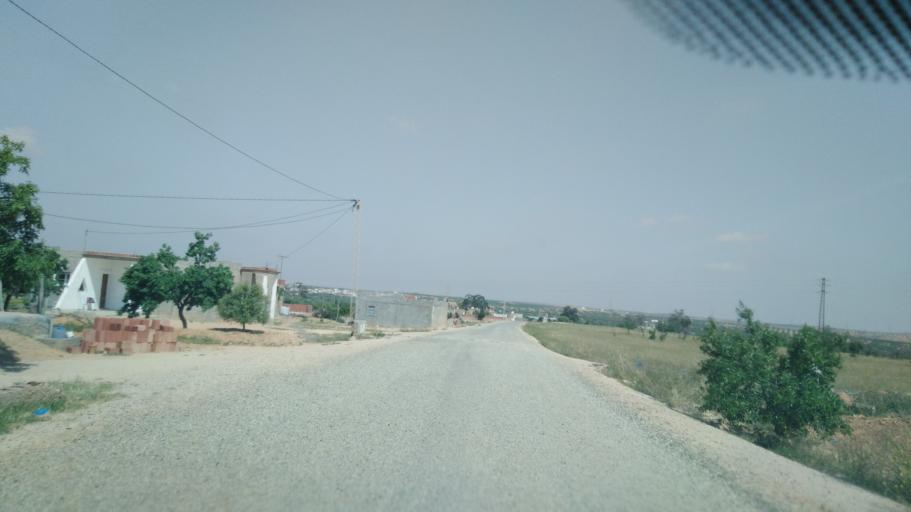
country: TN
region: Safaqis
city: Sfax
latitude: 34.7271
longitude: 10.5726
